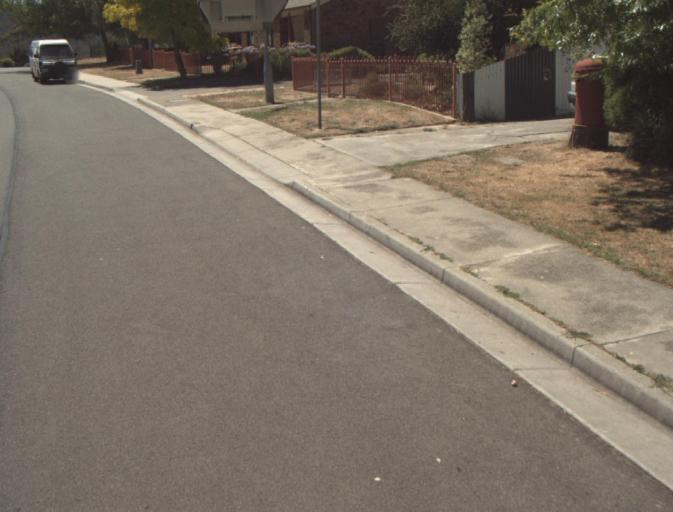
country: AU
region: Tasmania
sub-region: Launceston
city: Mayfield
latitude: -41.3764
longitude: 147.1374
